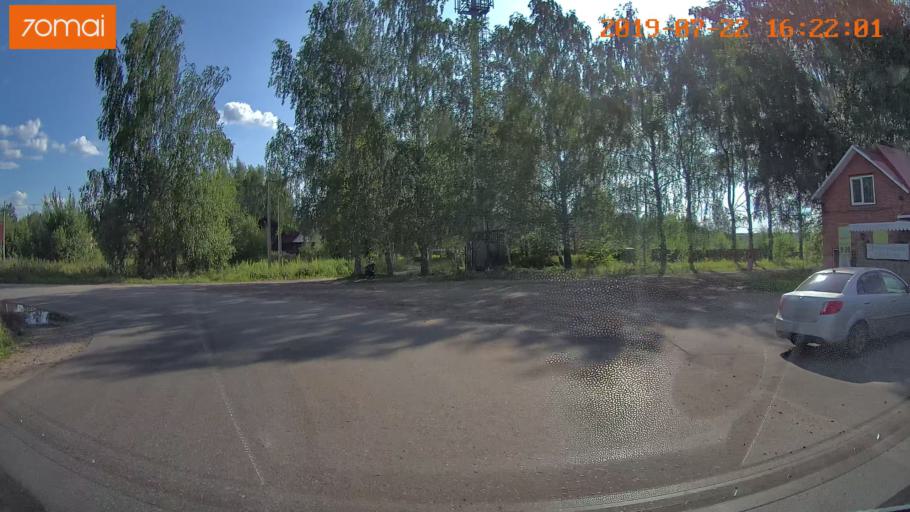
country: RU
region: Ivanovo
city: Novo-Talitsy
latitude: 57.0604
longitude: 40.8786
